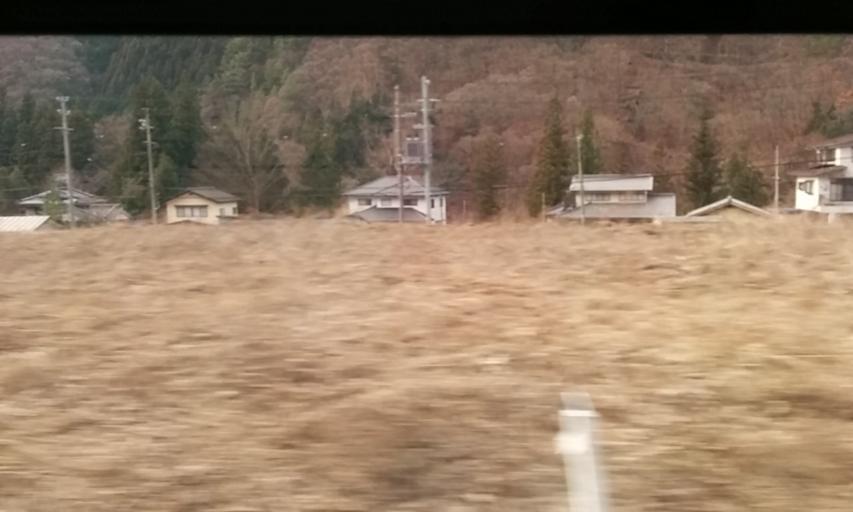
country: JP
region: Nagano
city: Shiojiri
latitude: 36.0516
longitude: 137.8963
